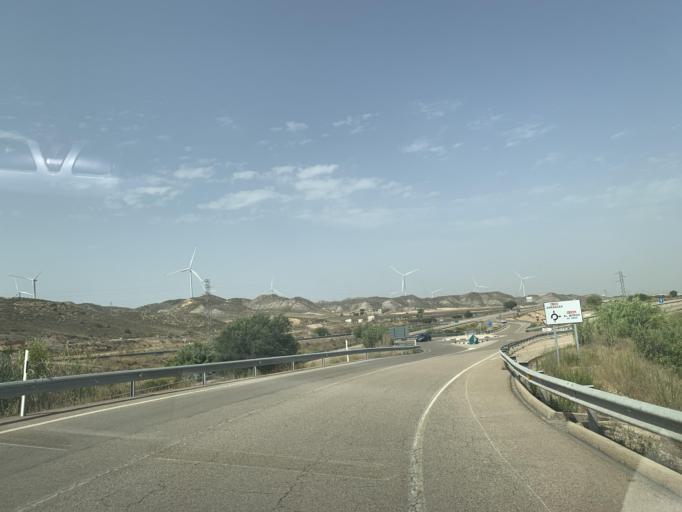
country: ES
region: Aragon
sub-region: Provincia de Zaragoza
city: El Burgo de Ebro
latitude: 41.5455
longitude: -0.6966
